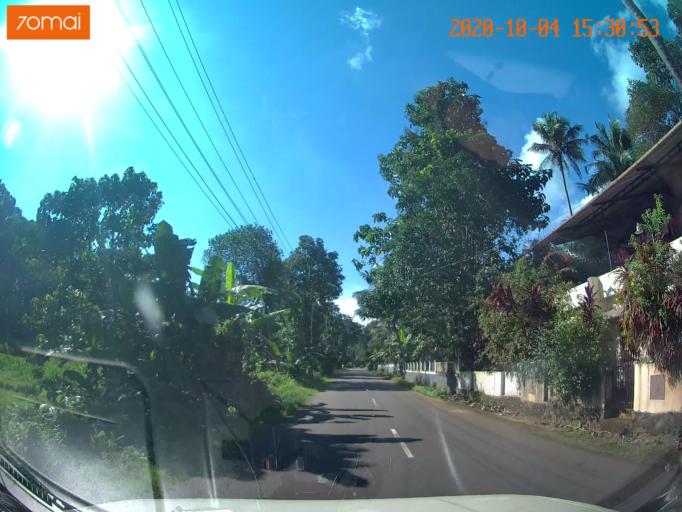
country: IN
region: Kerala
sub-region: Kottayam
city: Palackattumala
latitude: 9.7262
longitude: 76.6415
